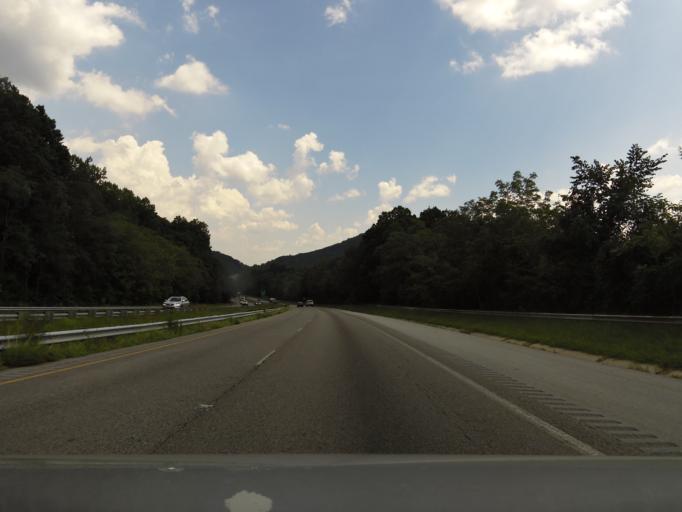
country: US
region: North Carolina
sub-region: Polk County
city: Columbus
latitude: 35.2539
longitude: -82.2371
